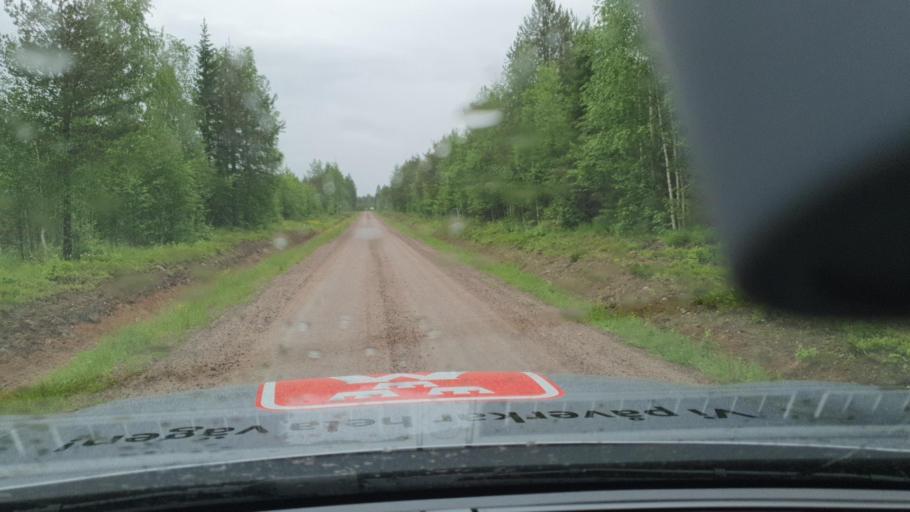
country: SE
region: Norrbotten
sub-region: Overkalix Kommun
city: OEverkalix
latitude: 66.5372
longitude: 22.7409
